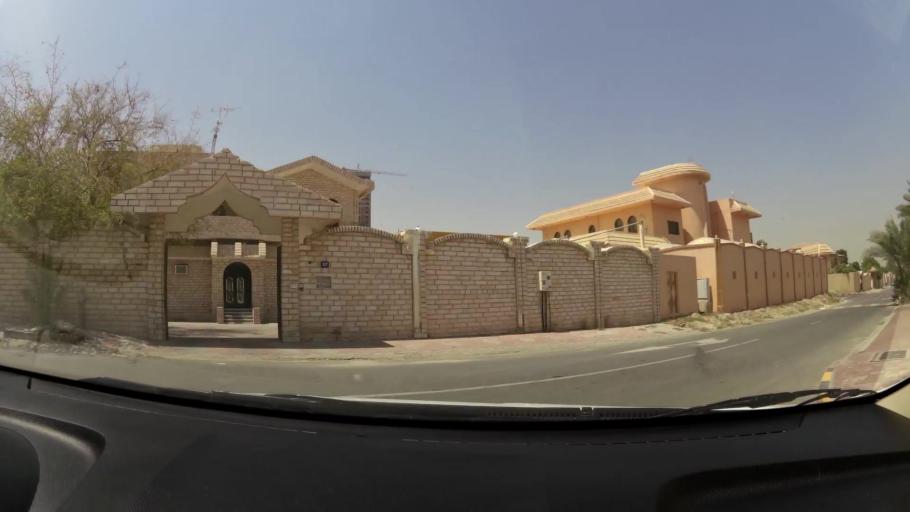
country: AE
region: Ajman
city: Ajman
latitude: 25.4013
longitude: 55.5129
